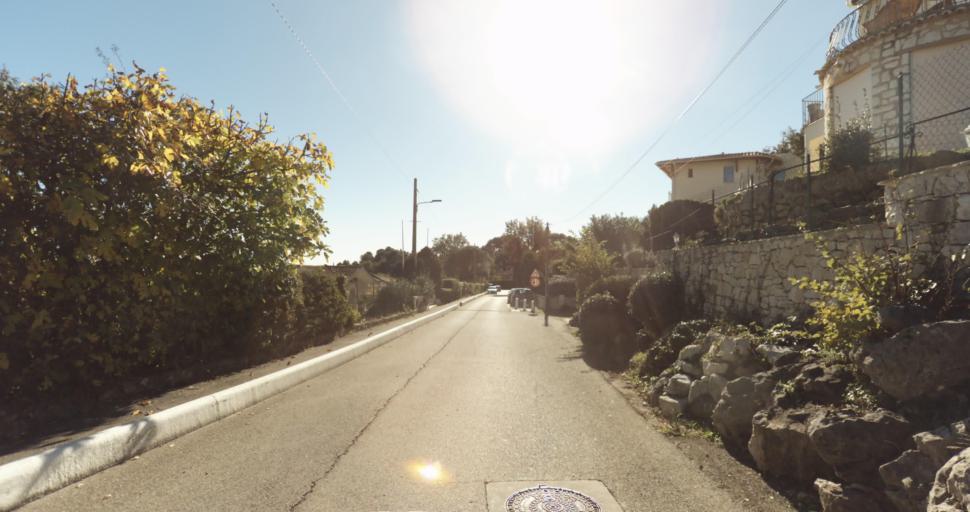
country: FR
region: Provence-Alpes-Cote d'Azur
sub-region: Departement des Alpes-Maritimes
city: Vence
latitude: 43.7180
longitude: 7.1118
